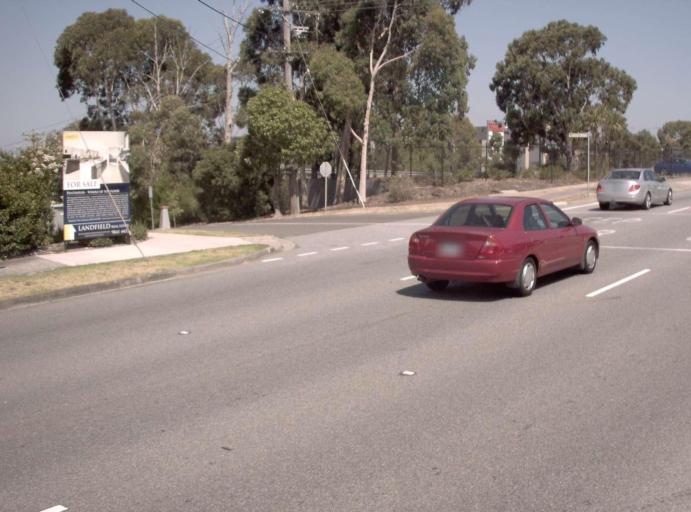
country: AU
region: Victoria
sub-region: Manningham
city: Doncaster
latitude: -37.7819
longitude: 145.1238
